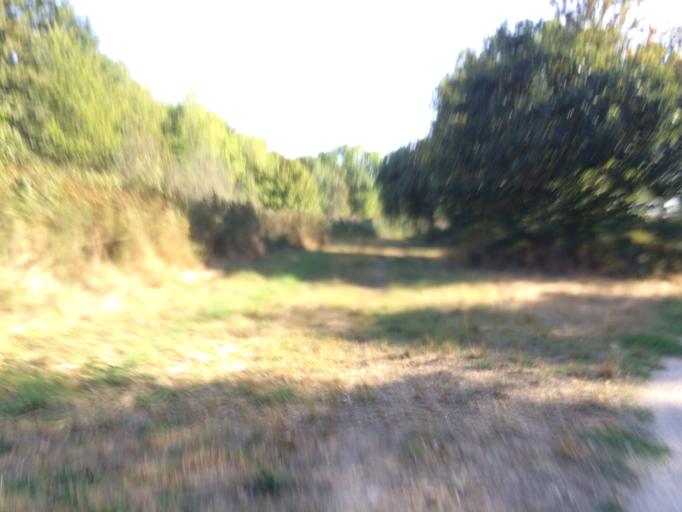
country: FR
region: Ile-de-France
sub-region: Departement de l'Essonne
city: Epinay-sur-Orge
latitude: 48.6643
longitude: 2.3179
